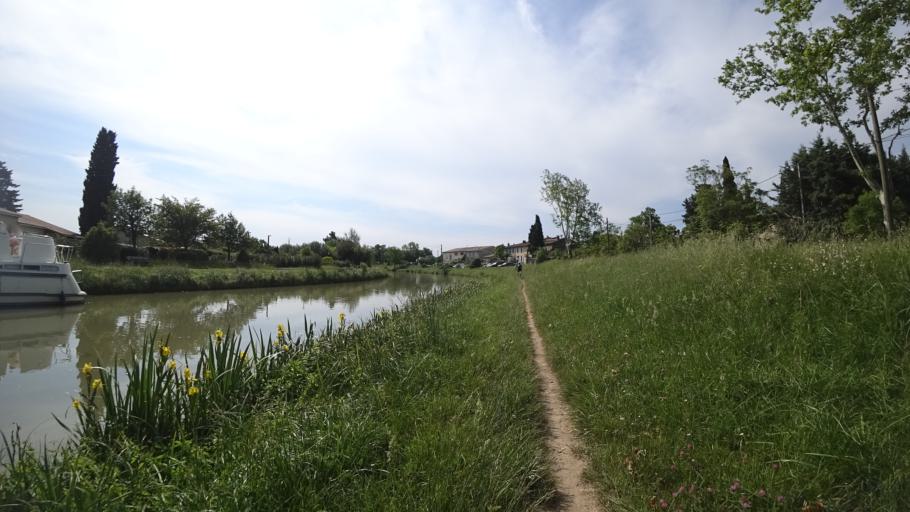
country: FR
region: Languedoc-Roussillon
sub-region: Departement de l'Aude
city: Lezignan-Corbieres
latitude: 43.2414
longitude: 2.7642
